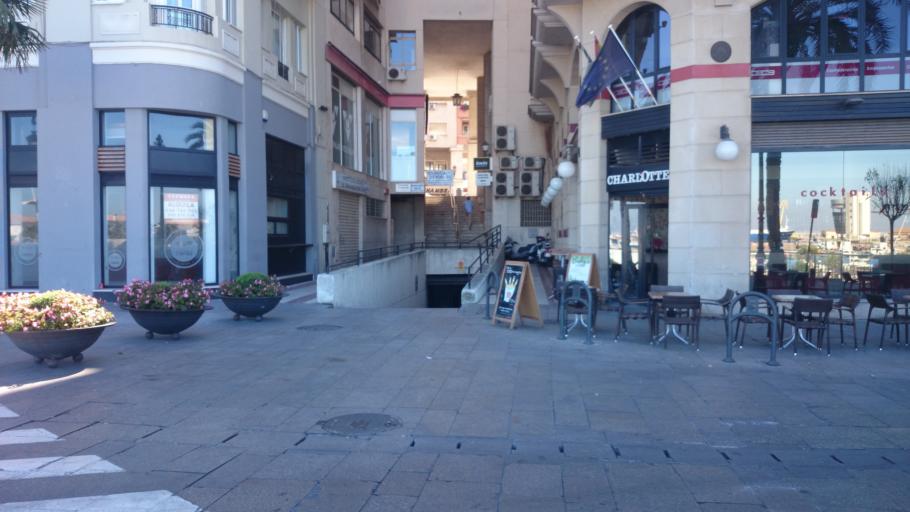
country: ES
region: Ceuta
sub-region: Ceuta
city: Ceuta
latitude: 35.8887
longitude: -5.3142
